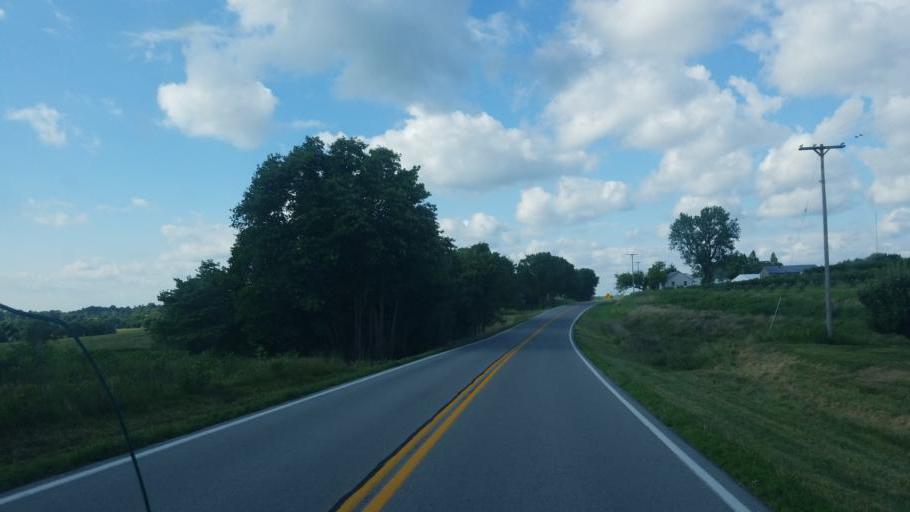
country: US
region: Illinois
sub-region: Union County
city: Cobden
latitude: 37.5918
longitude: -89.3236
